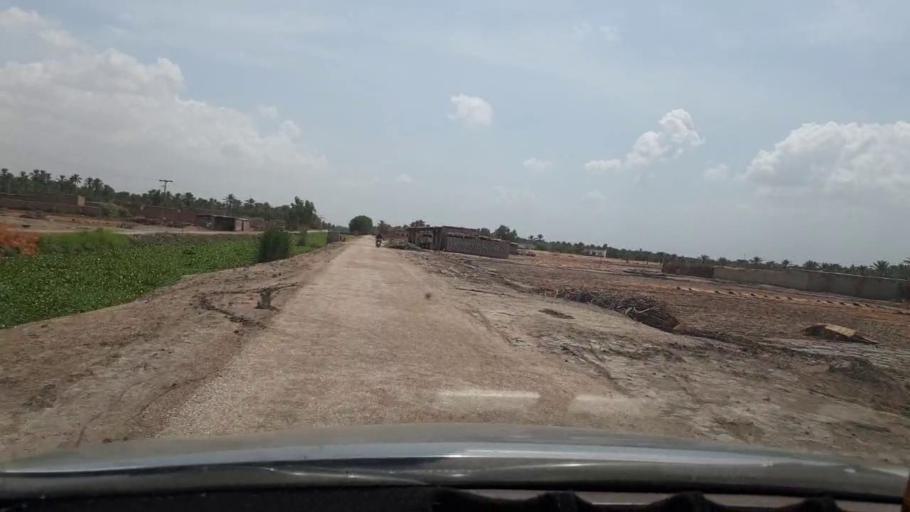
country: PK
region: Sindh
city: Khairpur
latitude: 27.4543
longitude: 68.7889
